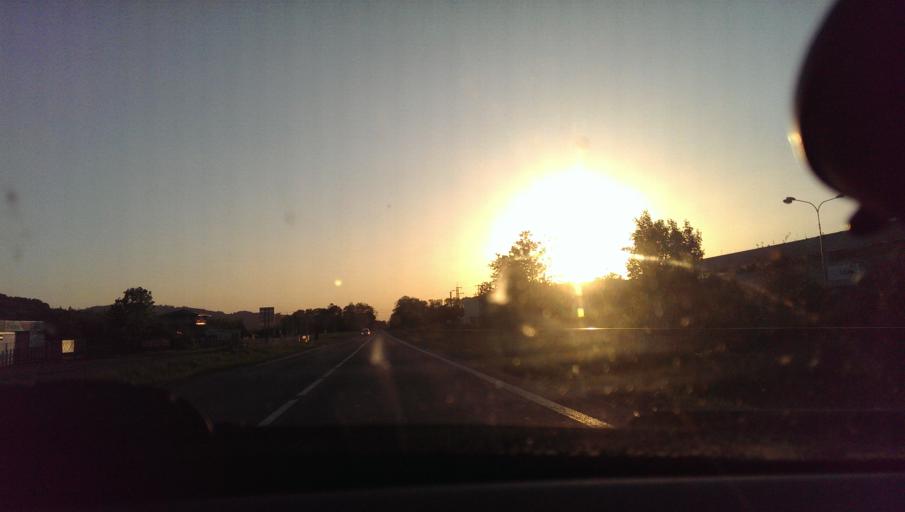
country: CZ
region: Zlin
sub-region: Okres Vsetin
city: Roznov pod Radhostem
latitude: 49.4599
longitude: 18.1175
